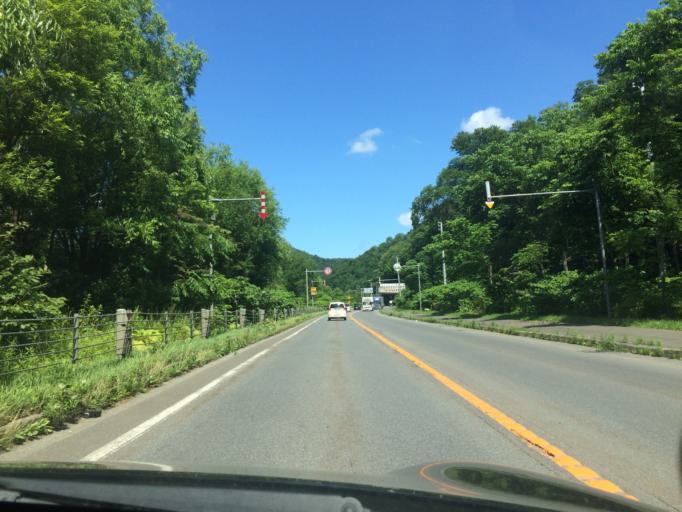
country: JP
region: Hokkaido
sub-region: Asahikawa-shi
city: Asahikawa
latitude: 43.7350
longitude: 142.2359
